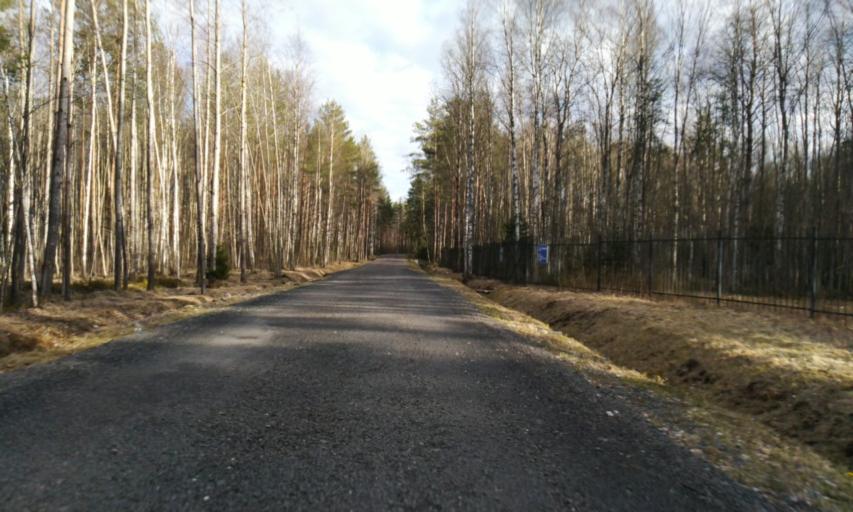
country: RU
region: Leningrad
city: Toksovo
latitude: 60.1219
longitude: 30.4756
